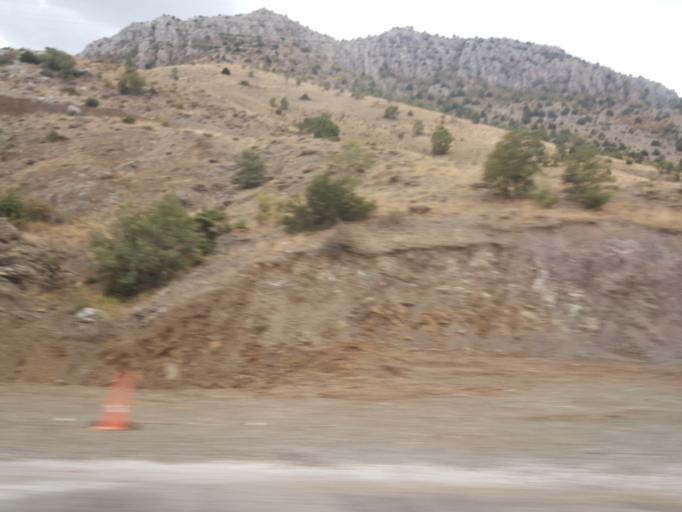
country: TR
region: Yozgat
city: Cekerek
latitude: 40.2088
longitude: 35.4770
